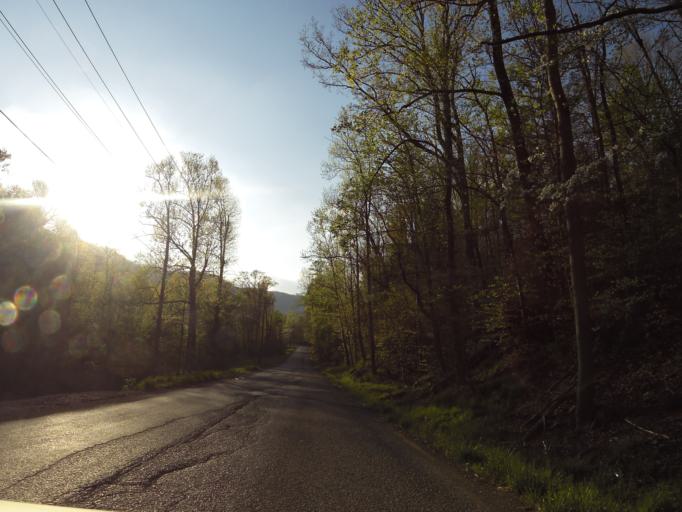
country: US
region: Kentucky
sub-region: Bell County
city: Middlesboro
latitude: 36.6104
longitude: -83.8211
